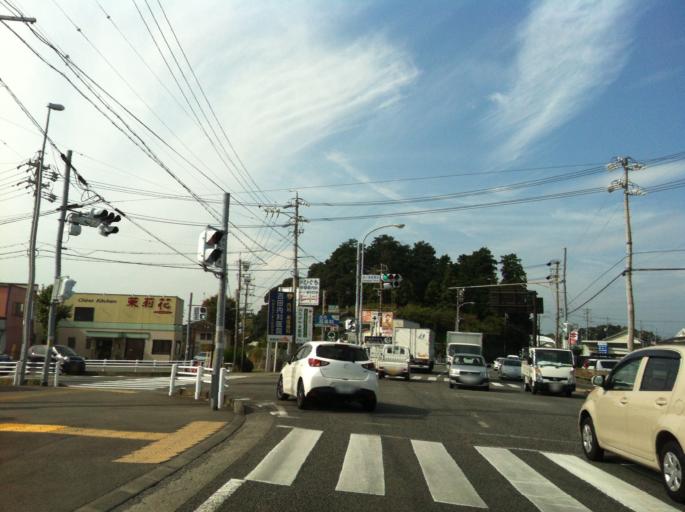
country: JP
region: Shizuoka
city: Kakegawa
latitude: 34.7777
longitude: 138.0285
